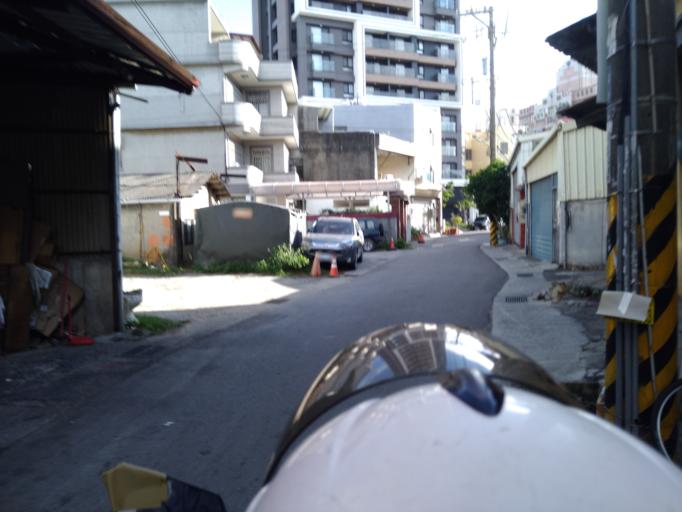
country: TW
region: Taiwan
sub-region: Hsinchu
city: Hsinchu
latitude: 24.8238
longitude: 120.9765
